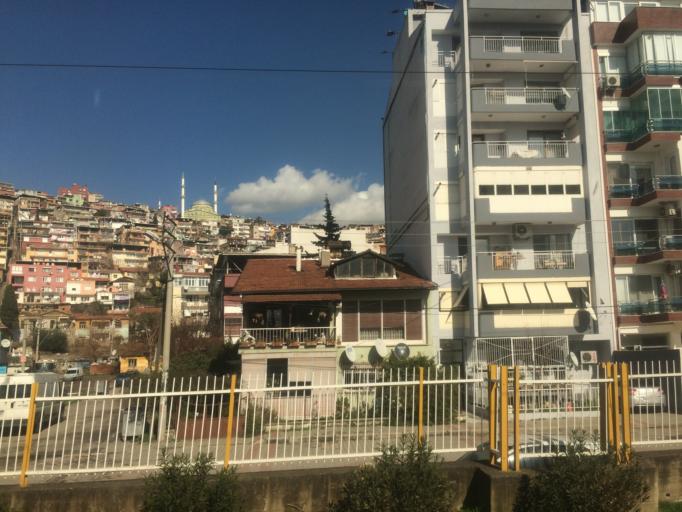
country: TR
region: Izmir
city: Karsiyaka
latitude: 38.4682
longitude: 27.1587
